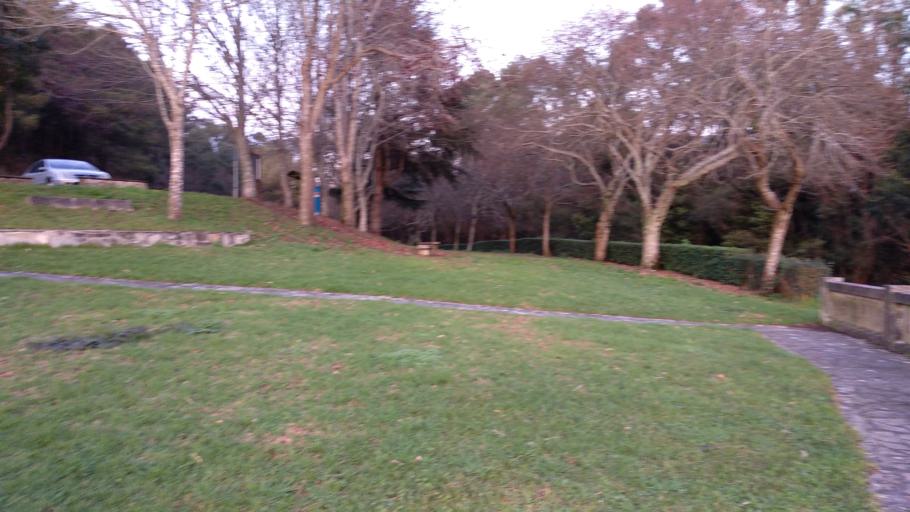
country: ES
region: Galicia
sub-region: Provincia de Pontevedra
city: Moana
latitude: 42.3096
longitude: -8.7326
